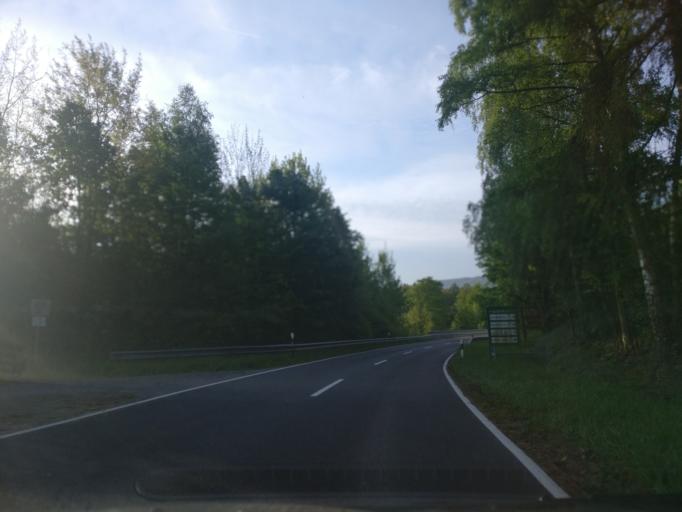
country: DE
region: Lower Saxony
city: Scheden
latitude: 51.4033
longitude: 9.7075
